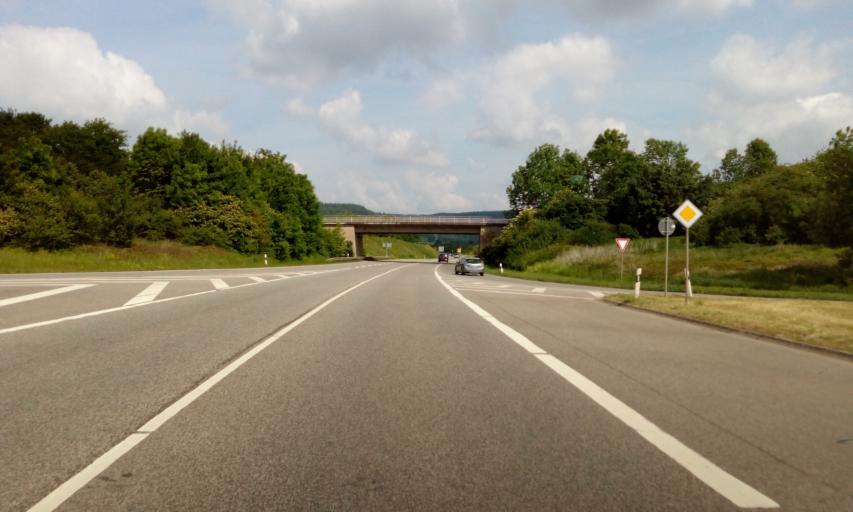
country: DE
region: Rheinland-Pfalz
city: Schweich
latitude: 49.8184
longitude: 6.7418
